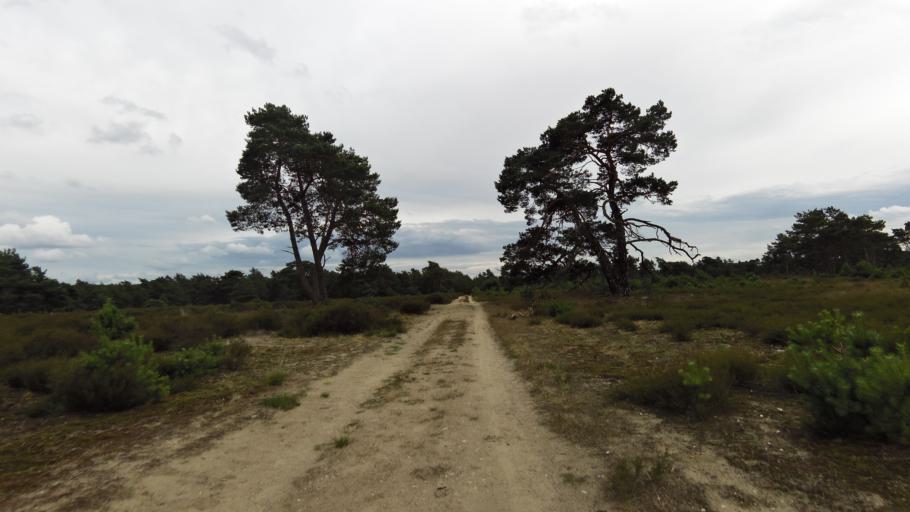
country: NL
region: Gelderland
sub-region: Gemeente Apeldoorn
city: Uddel
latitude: 52.2316
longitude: 5.8007
